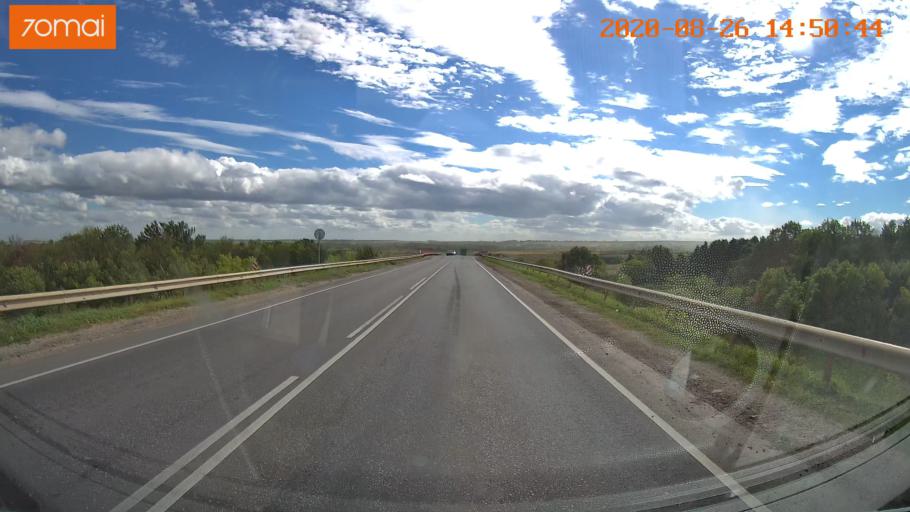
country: RU
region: Rjazan
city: Mikhaylov
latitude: 54.2419
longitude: 38.9842
